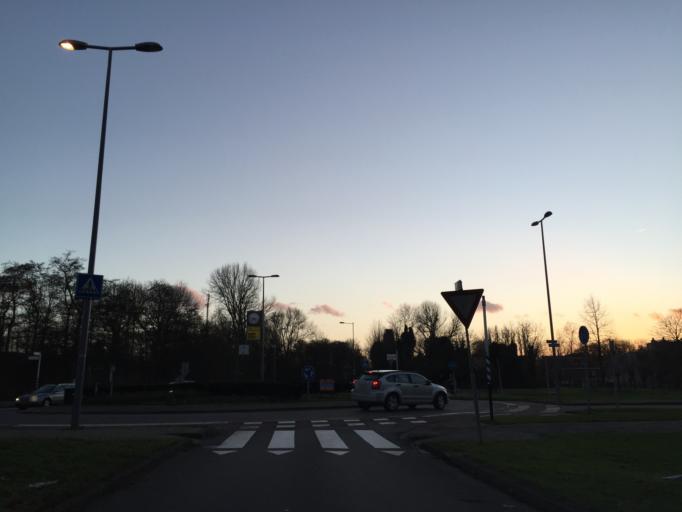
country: NL
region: South Holland
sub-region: Gemeente Lansingerland
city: Berkel en Rodenrijs
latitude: 51.9606
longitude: 4.4829
